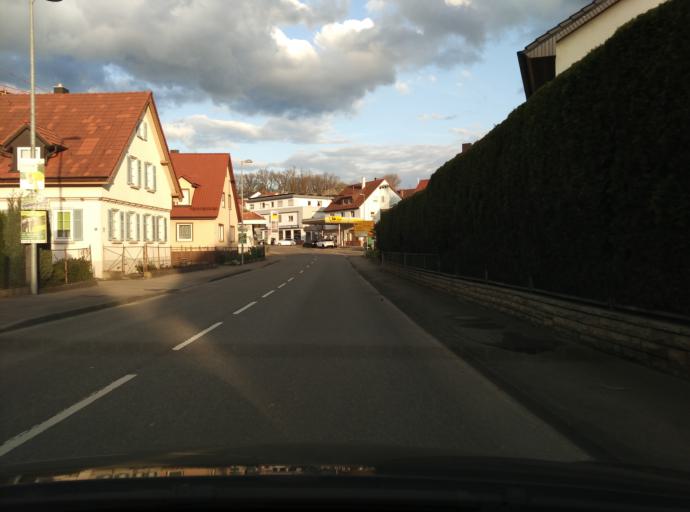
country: DE
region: Baden-Wuerttemberg
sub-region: Regierungsbezirk Stuttgart
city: Grossbettlingen
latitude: 48.5671
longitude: 9.3074
